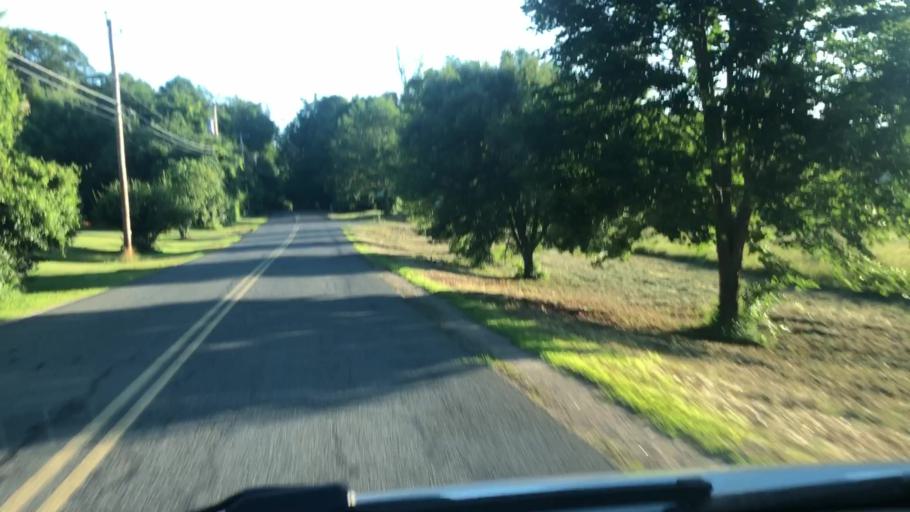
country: US
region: Massachusetts
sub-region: Hampshire County
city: Williamsburg
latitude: 42.3801
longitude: -72.7309
